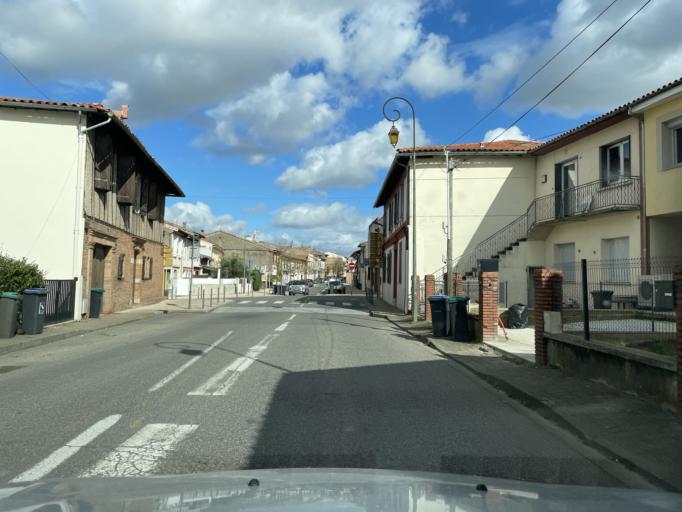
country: FR
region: Midi-Pyrenees
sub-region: Departement de la Haute-Garonne
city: Leguevin
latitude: 43.5996
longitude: 1.2321
